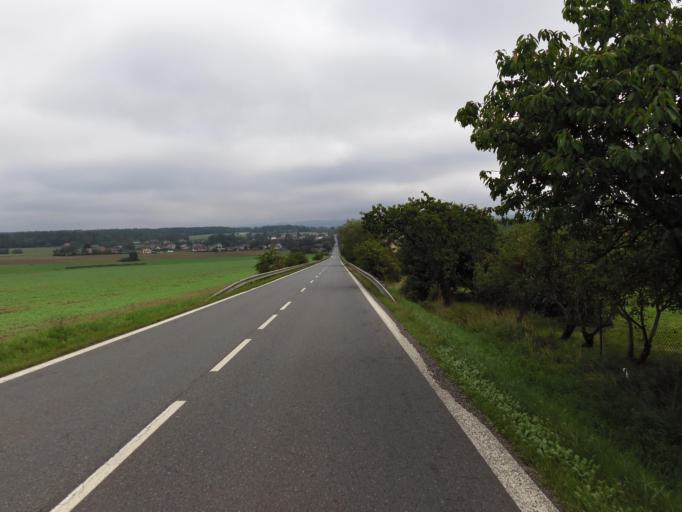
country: CZ
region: Jihocesky
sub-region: Okres Tabor
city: Sezimovo Usti
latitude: 49.4246
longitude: 14.7067
